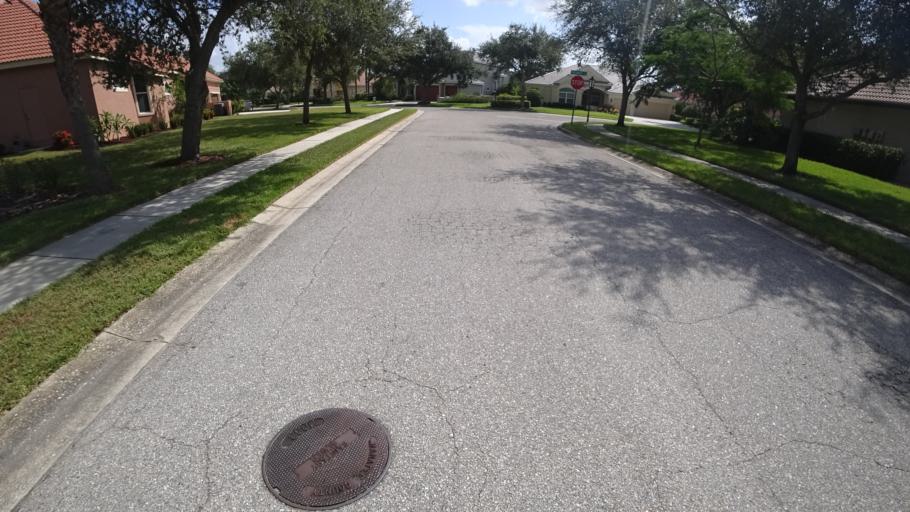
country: US
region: Florida
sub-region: Sarasota County
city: The Meadows
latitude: 27.4020
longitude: -82.4452
